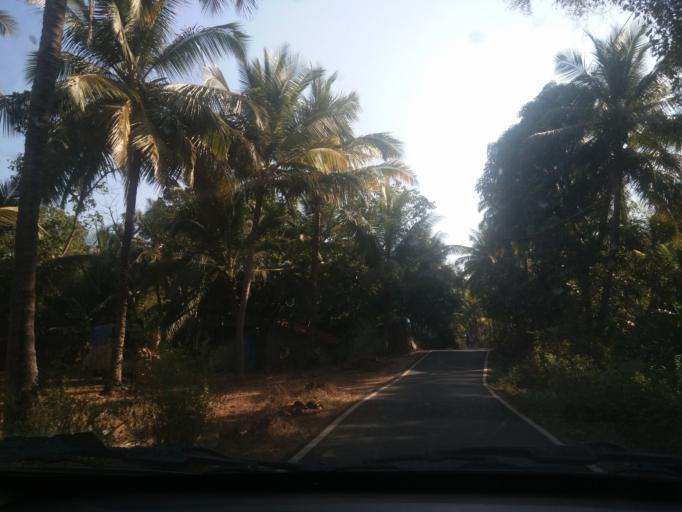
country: IN
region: Goa
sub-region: South Goa
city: Sancoale
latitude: 15.3479
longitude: 73.8902
